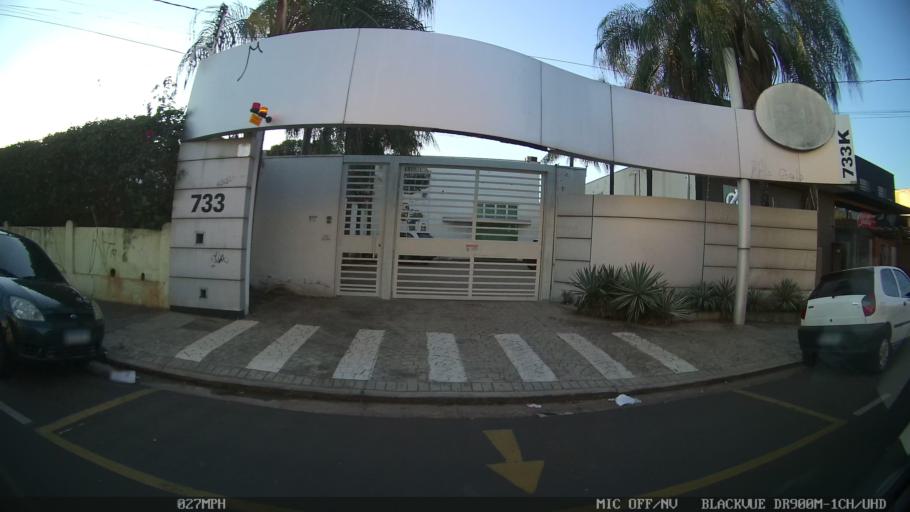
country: BR
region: Sao Paulo
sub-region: Sao Jose Do Rio Preto
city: Sao Jose do Rio Preto
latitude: -20.8046
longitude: -49.3666
